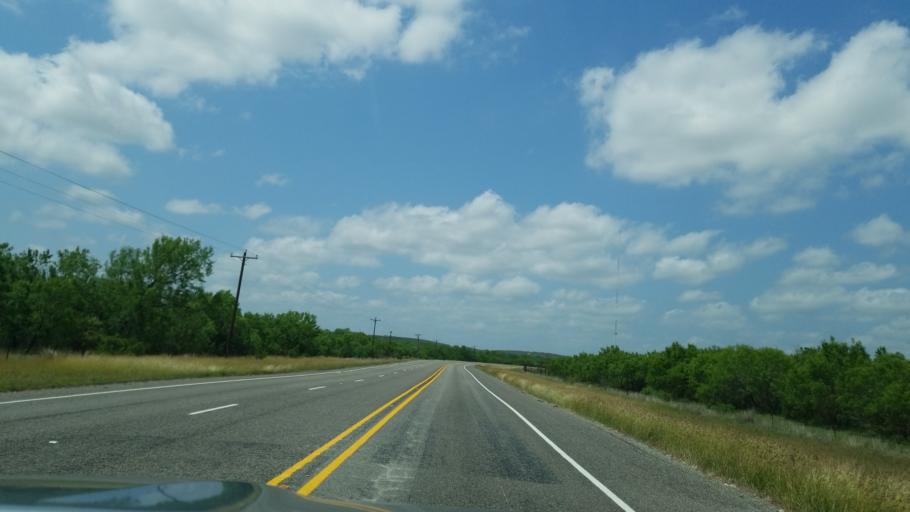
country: US
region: Texas
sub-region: Frio County
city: Pearsall
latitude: 28.9500
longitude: -99.2681
